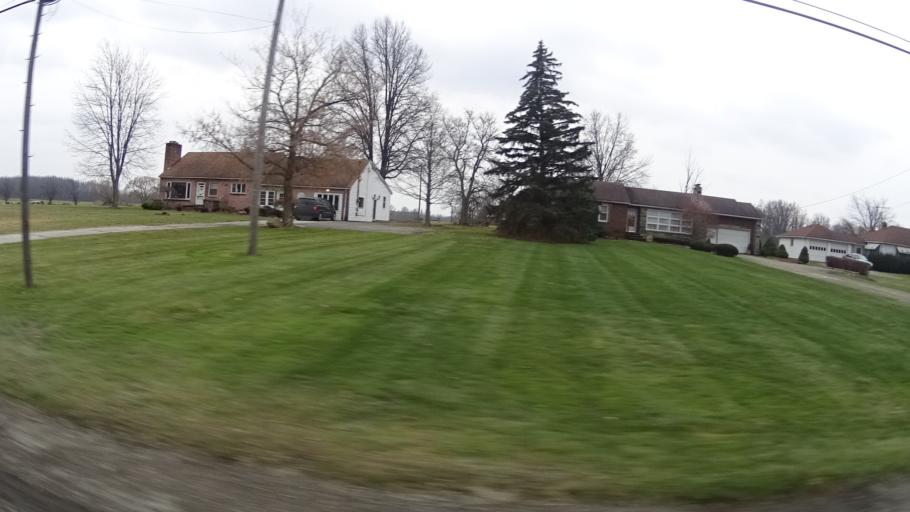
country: US
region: Ohio
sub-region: Lorain County
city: Amherst
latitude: 41.3680
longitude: -82.1871
